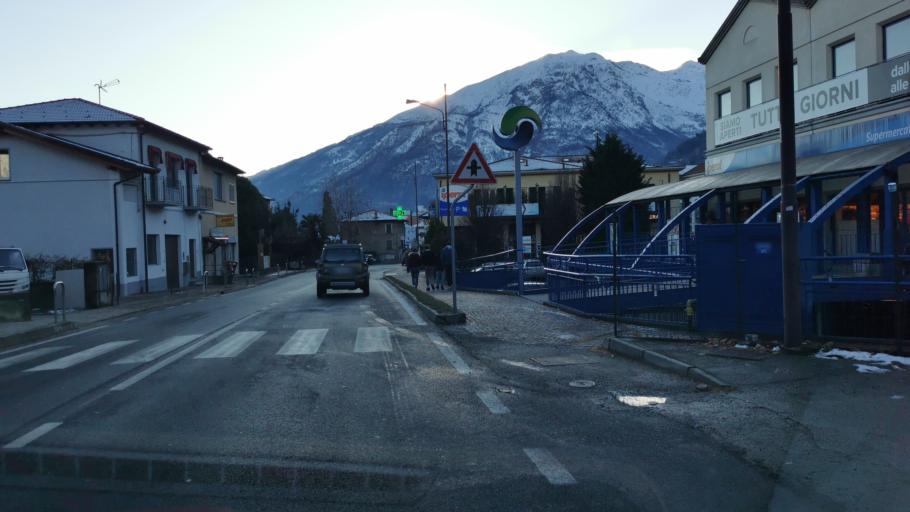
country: IT
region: Lombardy
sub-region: Provincia di Como
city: Consiglio di Rumo
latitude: 46.1430
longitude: 9.2962
